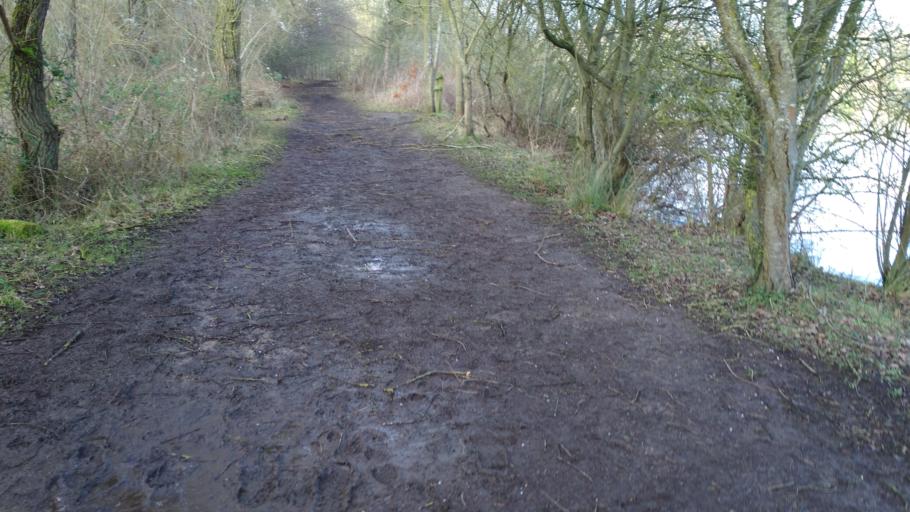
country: GB
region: England
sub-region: Oxfordshire
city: Radley
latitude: 51.6729
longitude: -1.2521
